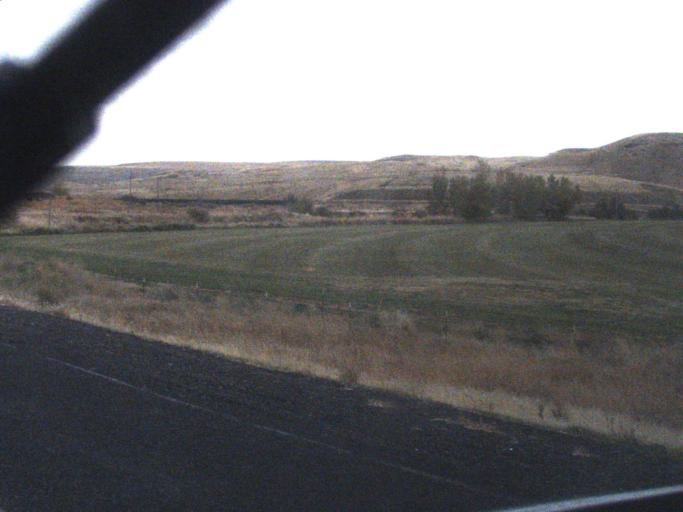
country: US
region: Washington
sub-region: Columbia County
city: Dayton
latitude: 46.7739
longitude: -118.0432
